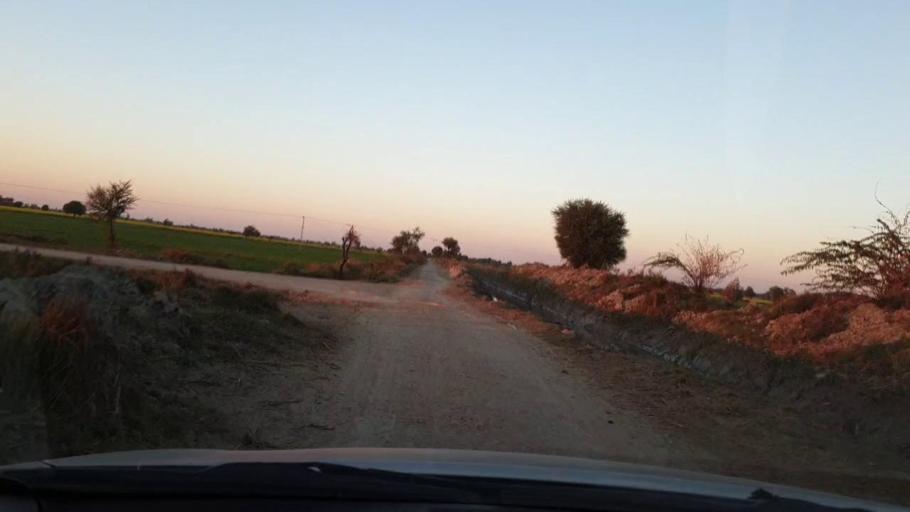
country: PK
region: Sindh
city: Jhol
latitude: 25.9038
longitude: 68.8861
